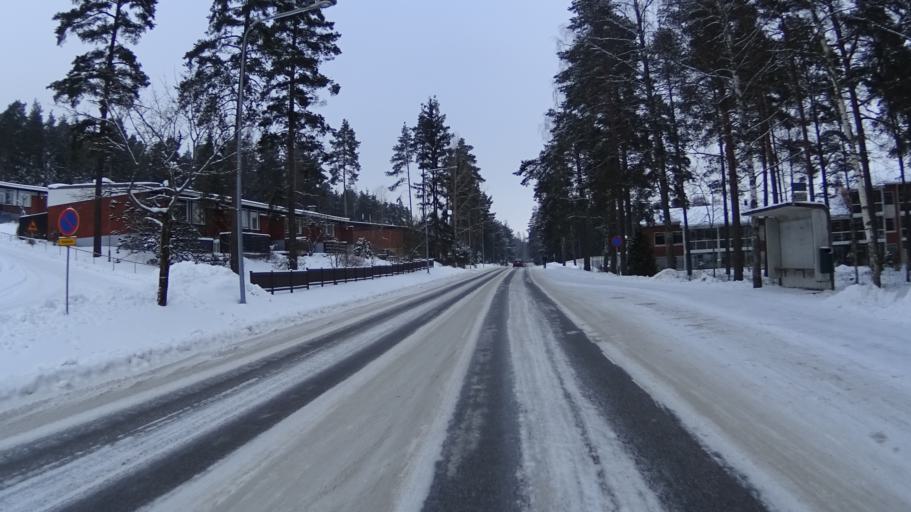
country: FI
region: Uusimaa
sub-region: Helsinki
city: Vihti
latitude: 60.3340
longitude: 24.3102
